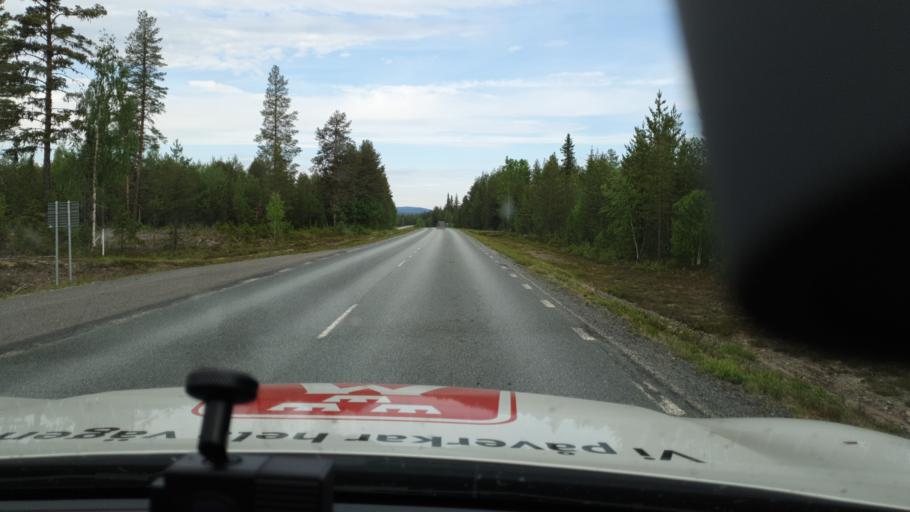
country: SE
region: Vaesterbotten
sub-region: Mala Kommun
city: Mala
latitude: 64.9976
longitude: 18.4801
